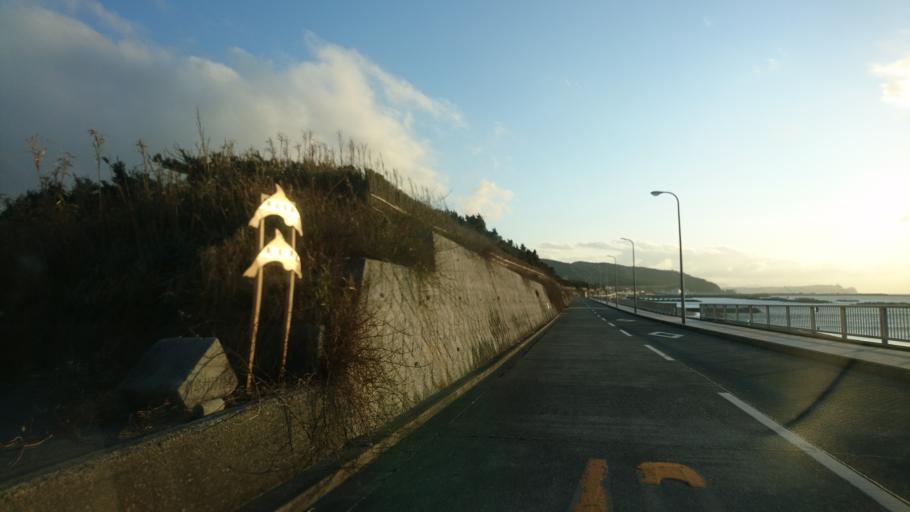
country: JP
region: Shizuoka
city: Shimoda
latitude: 34.3826
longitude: 139.2555
